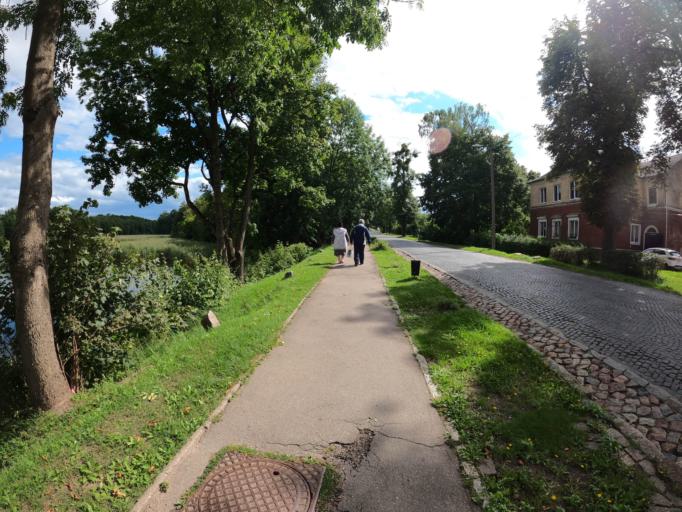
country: RU
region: Kaliningrad
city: Zheleznodorozhnyy
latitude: 54.3568
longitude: 21.3071
